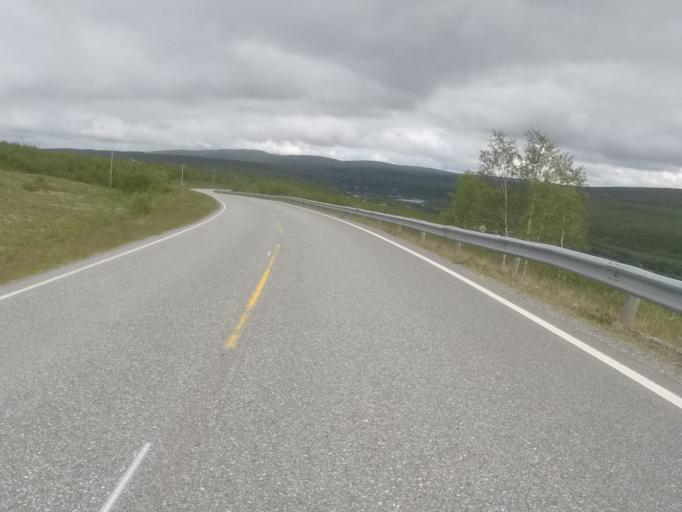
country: NO
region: Finnmark Fylke
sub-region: Alta
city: Alta
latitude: 69.4372
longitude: 23.6446
